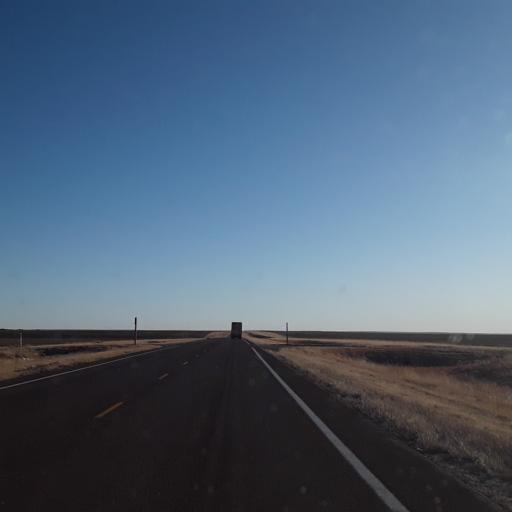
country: US
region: Kansas
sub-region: Sherman County
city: Goodland
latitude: 39.1489
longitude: -101.7268
